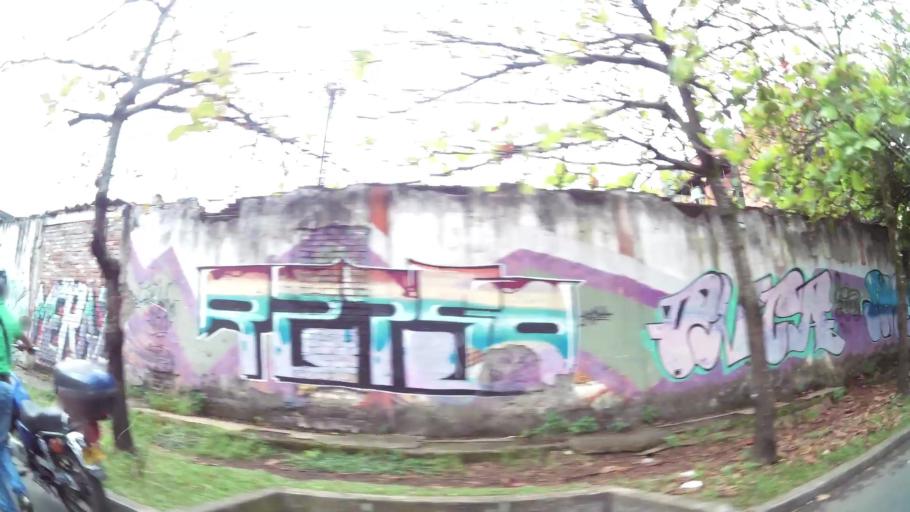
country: CO
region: Valle del Cauca
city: Cali
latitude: 3.3930
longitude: -76.5330
